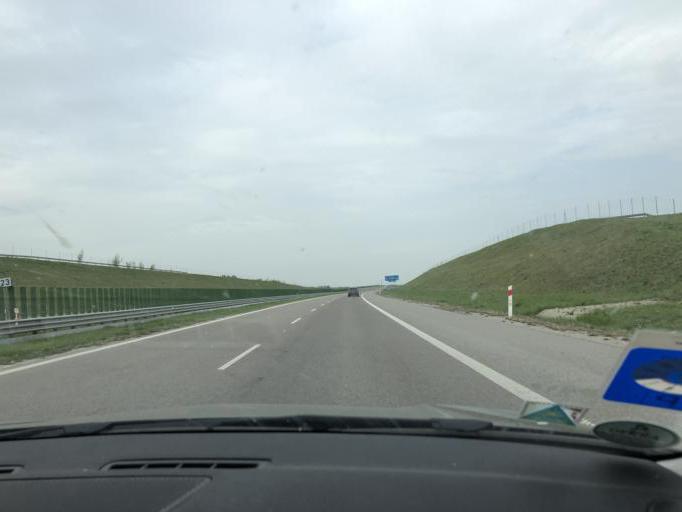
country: PL
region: Subcarpathian Voivodeship
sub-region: Powiat przeworski
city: Mirocin
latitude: 50.0314
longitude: 22.5748
